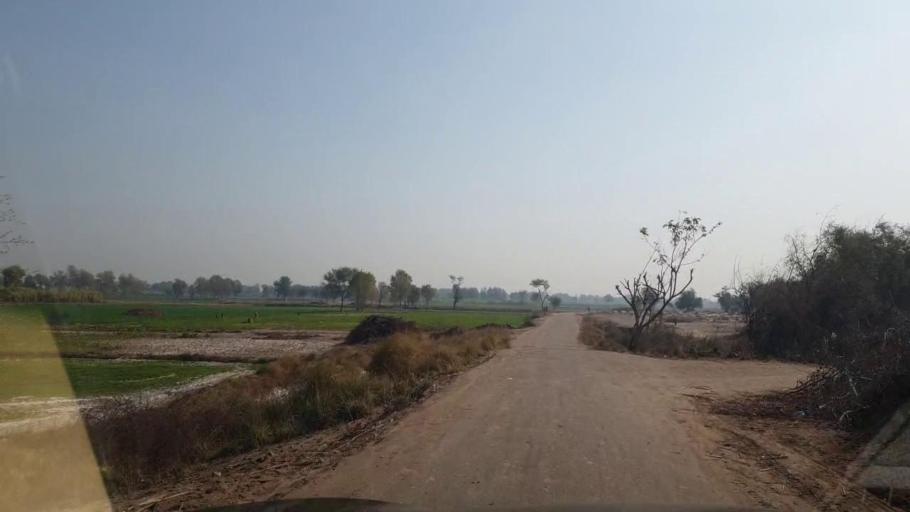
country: PK
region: Sindh
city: Ubauro
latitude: 28.1314
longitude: 69.7649
